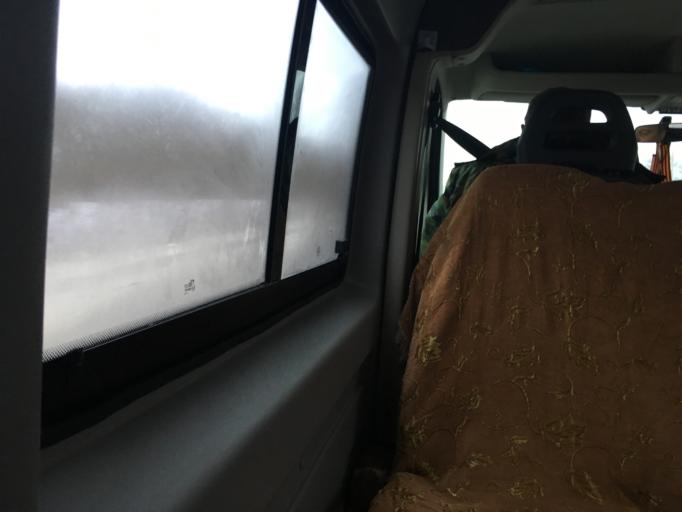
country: RU
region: Tula
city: Dubna
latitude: 54.0677
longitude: 37.0425
